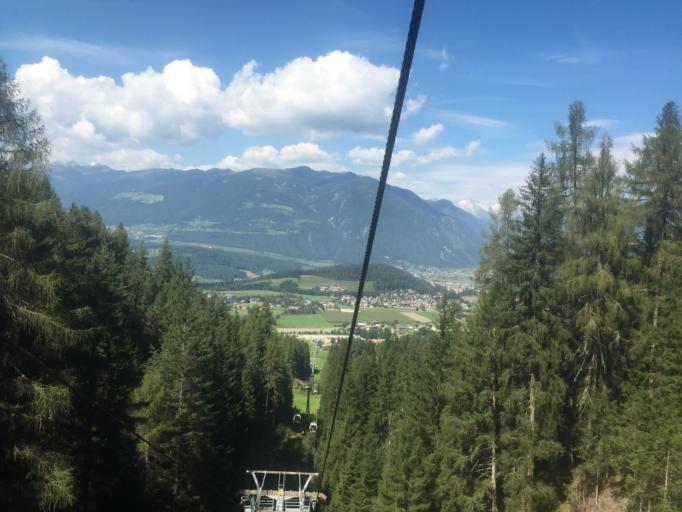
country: IT
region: Trentino-Alto Adige
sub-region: Bolzano
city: Riscone
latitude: 46.7620
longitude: 11.9459
